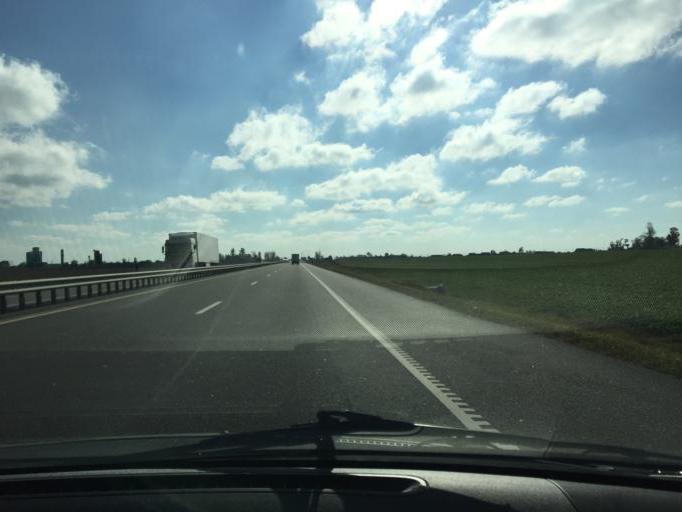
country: BY
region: Minsk
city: Slutsk
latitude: 53.1133
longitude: 27.5663
